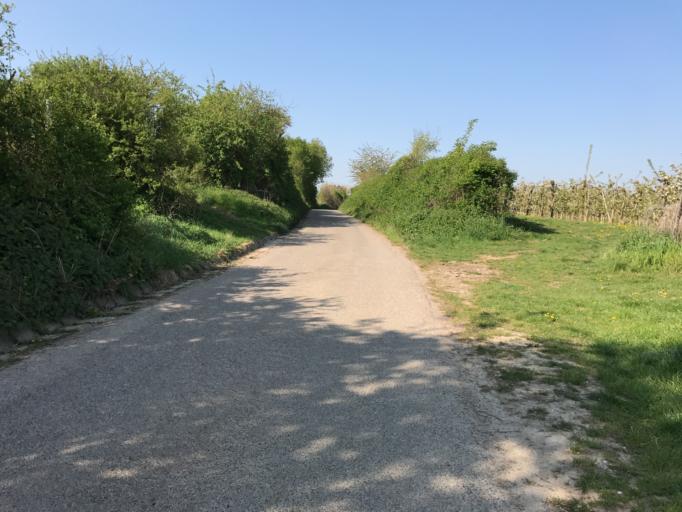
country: DE
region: Rheinland-Pfalz
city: Ober-Olm
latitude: 49.9725
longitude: 8.1841
